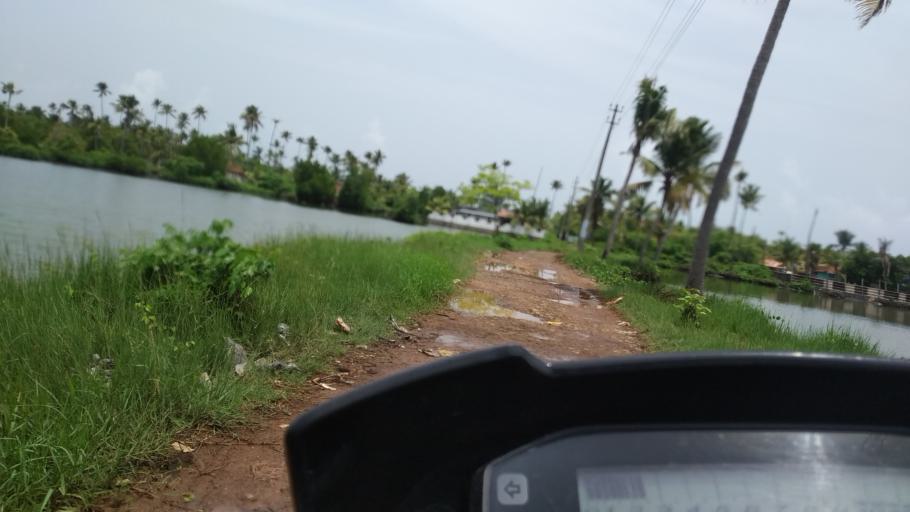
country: IN
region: Kerala
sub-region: Ernakulam
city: Elur
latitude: 10.0639
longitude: 76.2019
